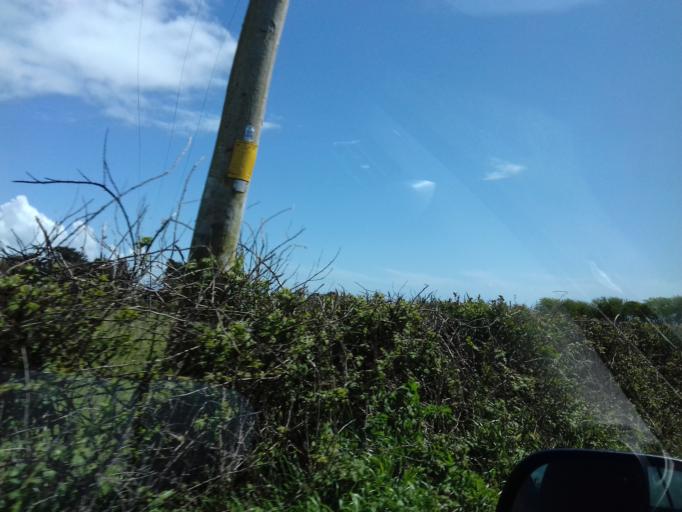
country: IE
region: Munster
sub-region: Waterford
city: Dunmore East
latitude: 52.1970
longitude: -6.8556
